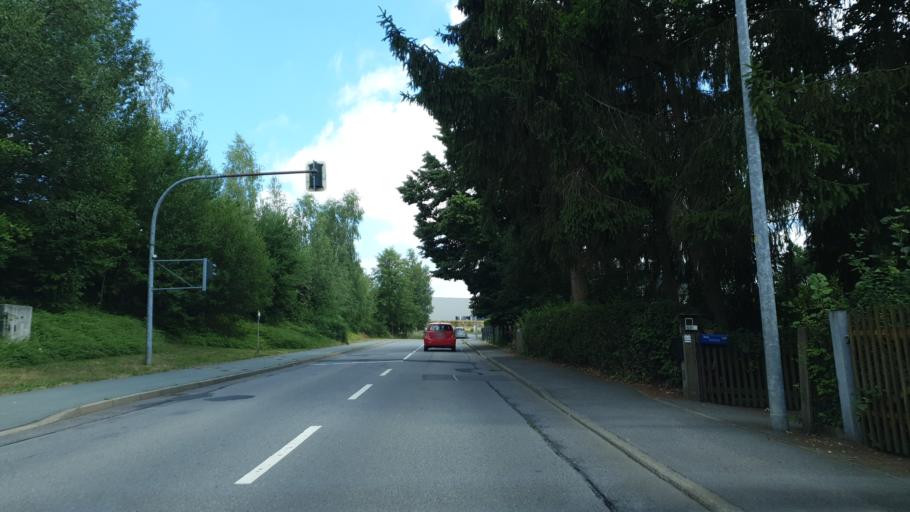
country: DE
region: Saxony
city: Neukirchen
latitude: 50.8026
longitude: 12.8451
